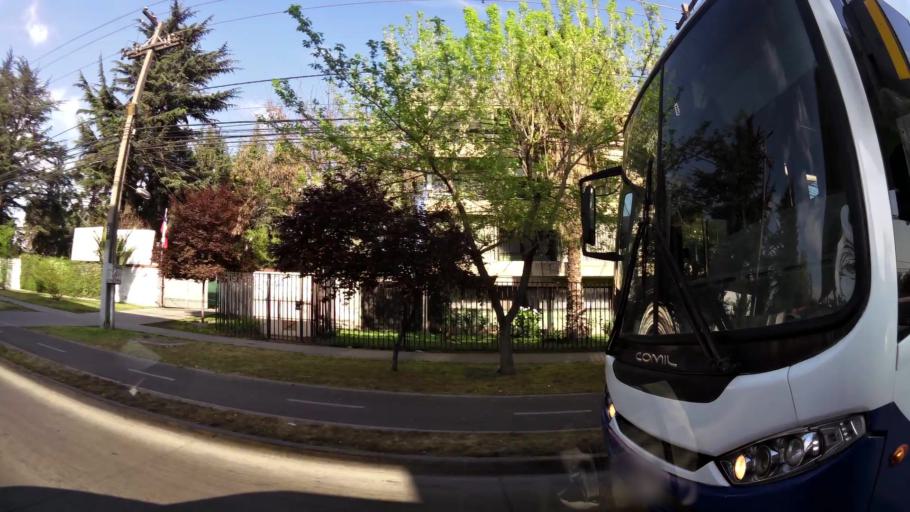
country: CL
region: Santiago Metropolitan
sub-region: Provincia de Cordillera
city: Puente Alto
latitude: -33.5584
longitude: -70.5859
